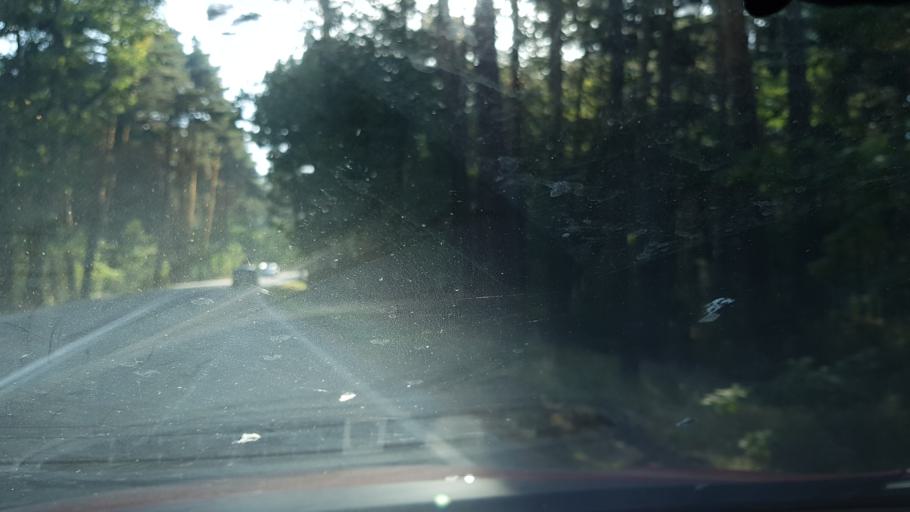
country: ES
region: Castille and Leon
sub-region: Provincia de Segovia
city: San Ildefonso
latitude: 40.8663
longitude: -4.0251
